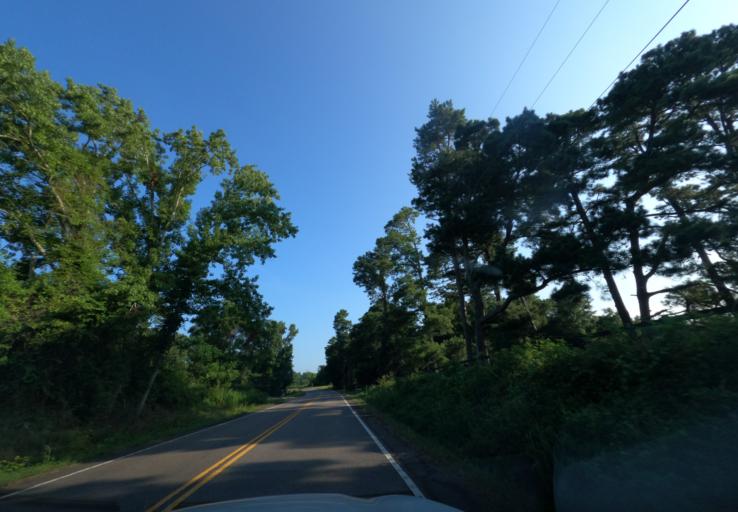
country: US
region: South Carolina
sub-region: Edgefield County
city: Murphys Estates
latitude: 33.6193
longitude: -81.9683
